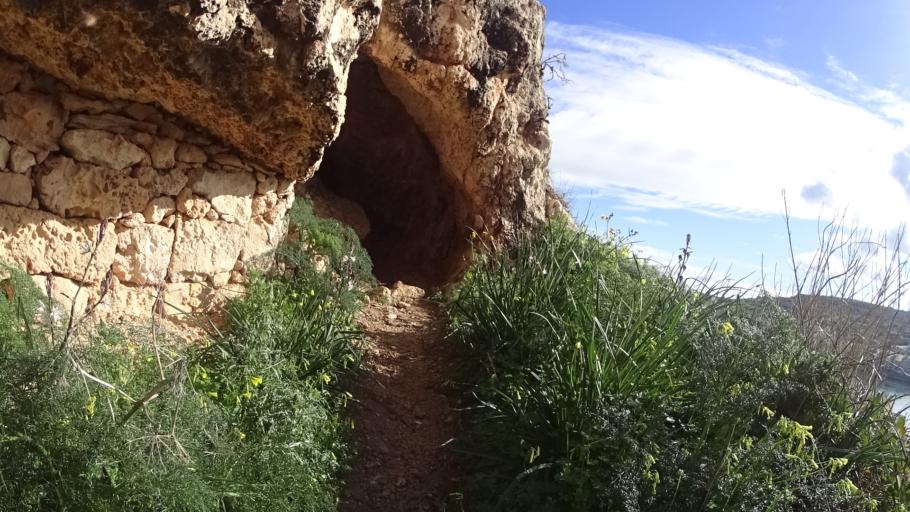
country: MT
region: Il-Mellieha
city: Mellieha
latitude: 35.9485
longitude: 14.3808
